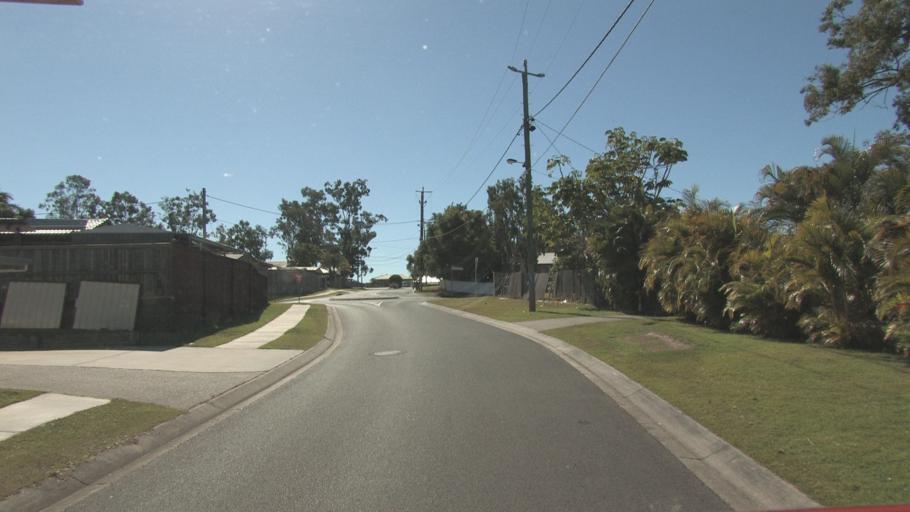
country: AU
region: Queensland
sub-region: Logan
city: Park Ridge South
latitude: -27.6887
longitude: 153.0270
